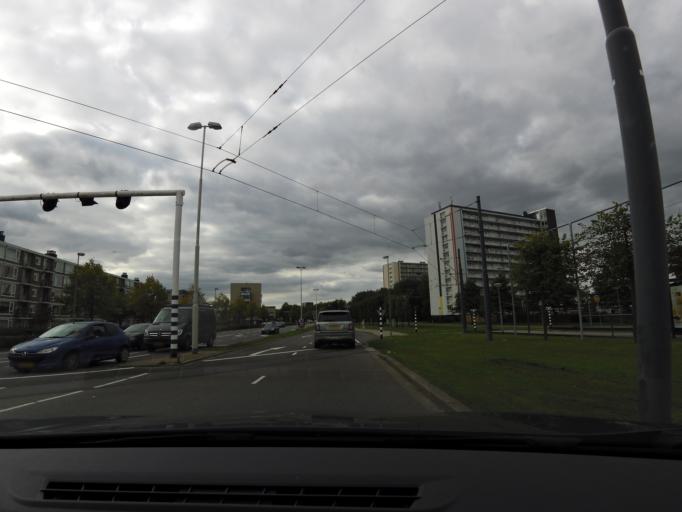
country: NL
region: South Holland
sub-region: Gemeente Schiedam
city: Schiedam
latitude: 51.9231
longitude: 4.4026
